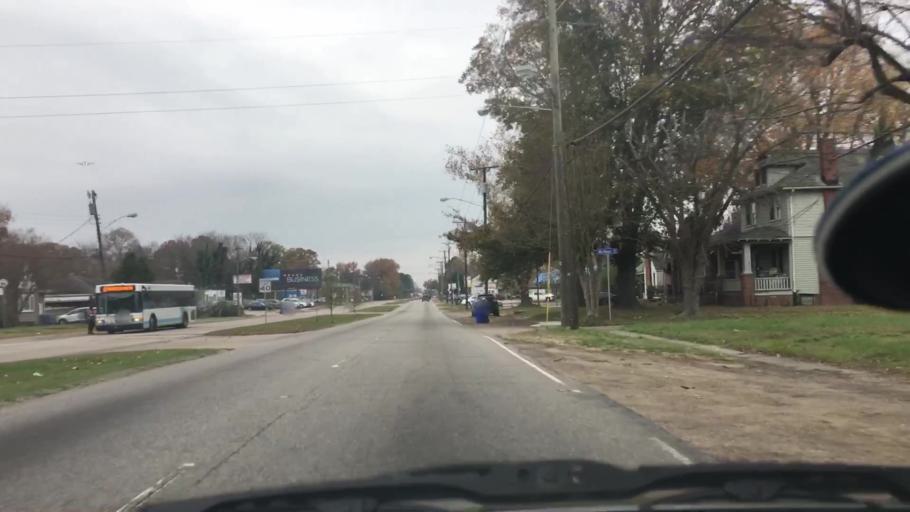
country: US
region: Virginia
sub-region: City of Norfolk
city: Norfolk
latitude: 36.8711
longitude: -76.2236
